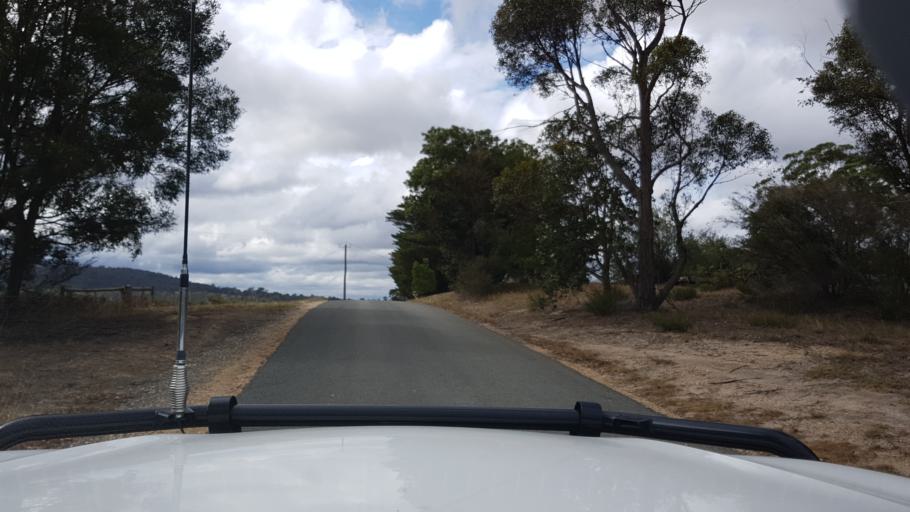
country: AU
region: Victoria
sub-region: East Gippsland
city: Bairnsdale
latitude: -37.7853
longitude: 147.5248
